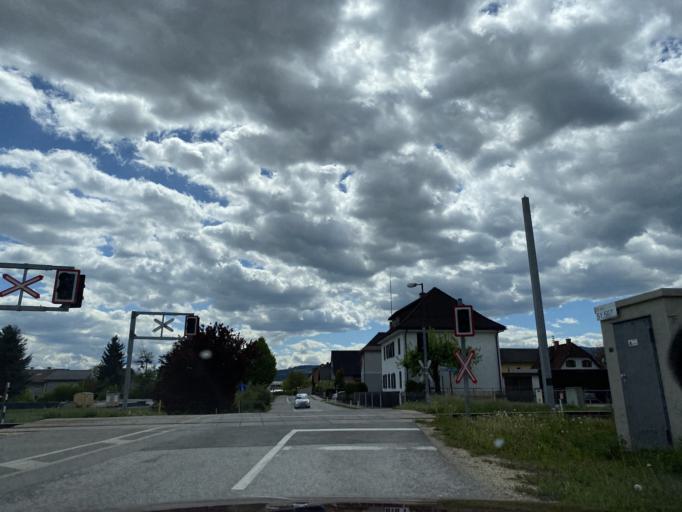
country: AT
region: Carinthia
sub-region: Politischer Bezirk Wolfsberg
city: Wolfsberg
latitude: 46.8325
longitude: 14.8375
